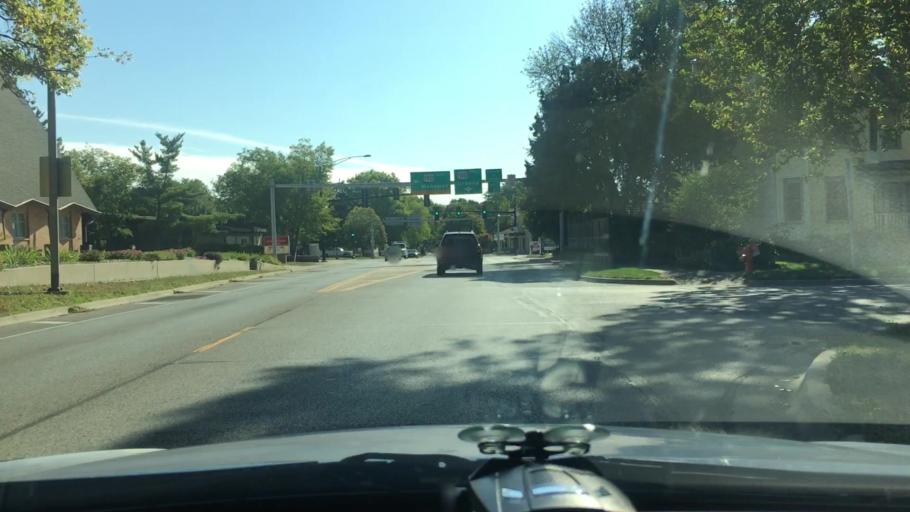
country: US
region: Illinois
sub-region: Champaign County
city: Champaign
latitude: 40.1126
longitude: -88.2591
